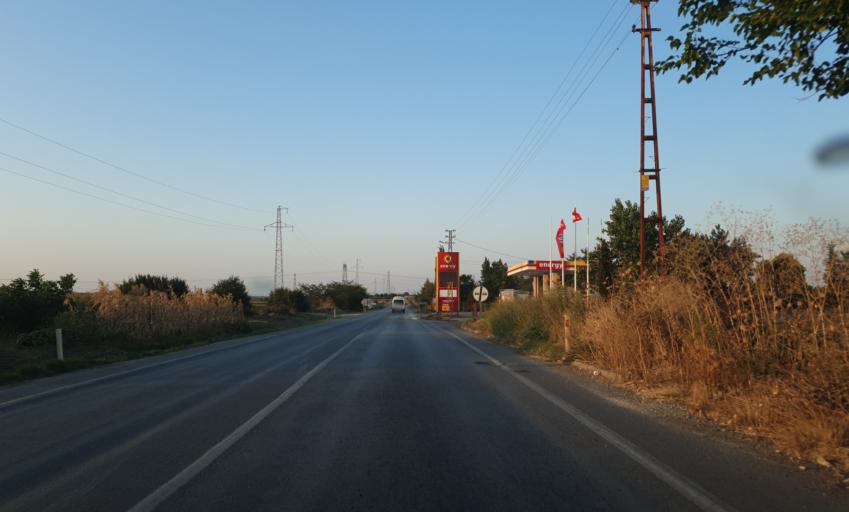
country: TR
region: Kirklareli
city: Luleburgaz
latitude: 41.4681
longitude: 27.3933
